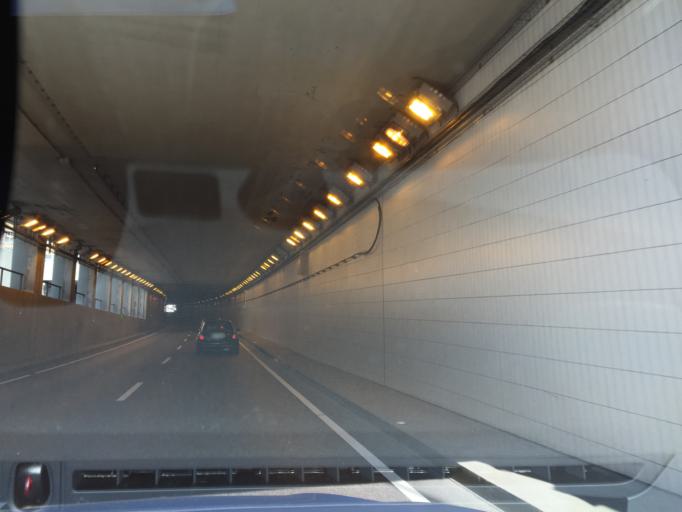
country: DE
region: Baden-Wuerttemberg
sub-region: Tuebingen Region
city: Ulm
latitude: 48.3923
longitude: 9.9830
